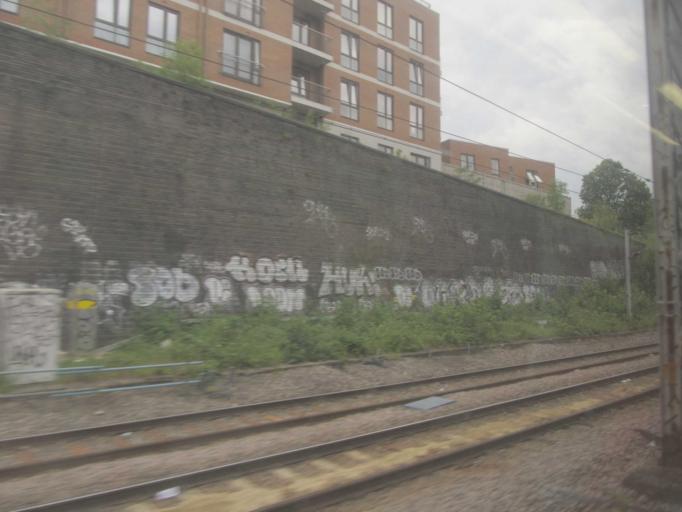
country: GB
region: England
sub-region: Greater London
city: Belsize Park
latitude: 51.5507
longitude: -0.2036
